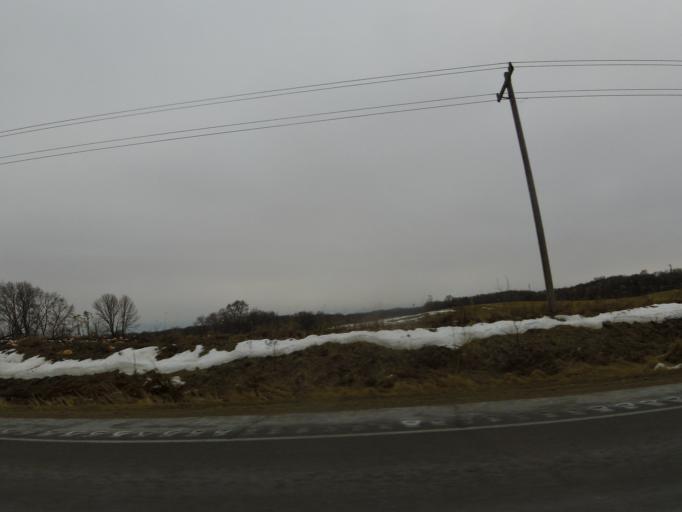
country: US
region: Minnesota
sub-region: Carver County
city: Cologne
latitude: 44.7760
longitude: -93.7185
